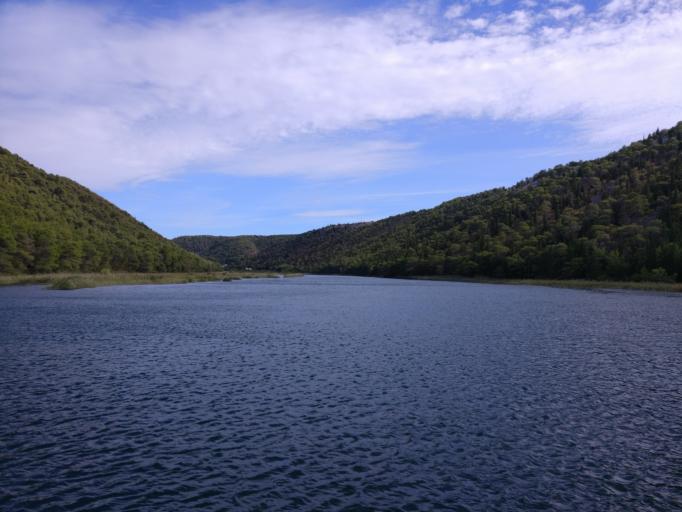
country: HR
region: Sibensko-Kniniska
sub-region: Grad Sibenik
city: Sibenik
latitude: 43.8181
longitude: 15.9492
